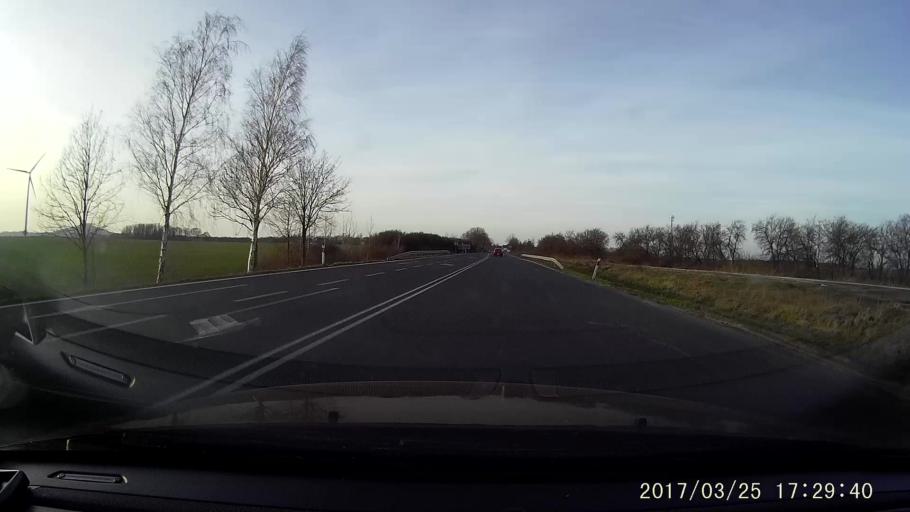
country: PL
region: Lower Silesian Voivodeship
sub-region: Powiat zgorzelecki
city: Sulikow
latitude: 51.0852
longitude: 15.0236
